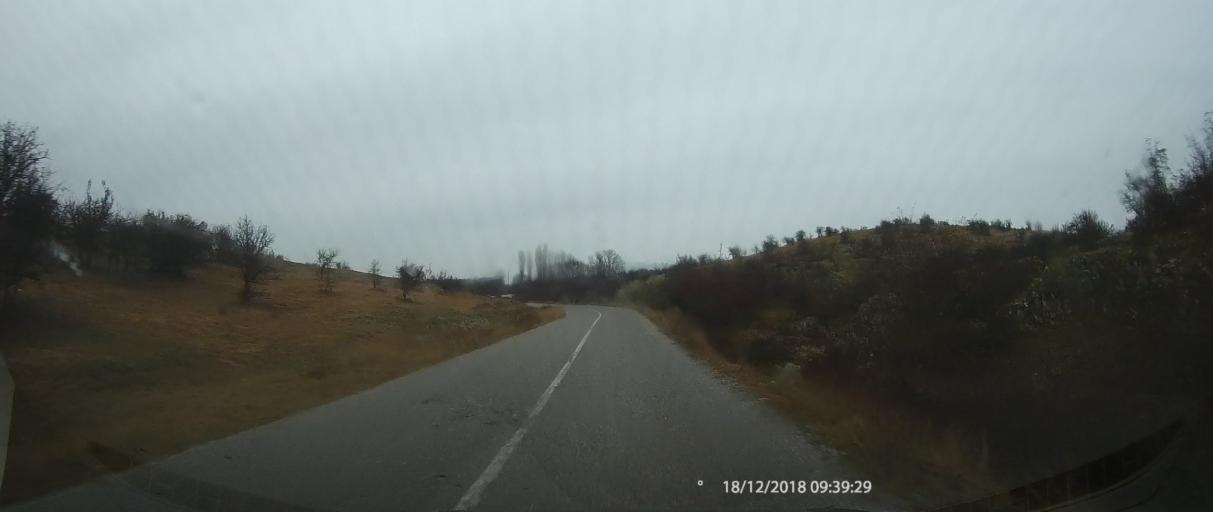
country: GR
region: Thessaly
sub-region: Nomos Larisis
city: Elassona
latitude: 39.9996
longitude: 22.2167
